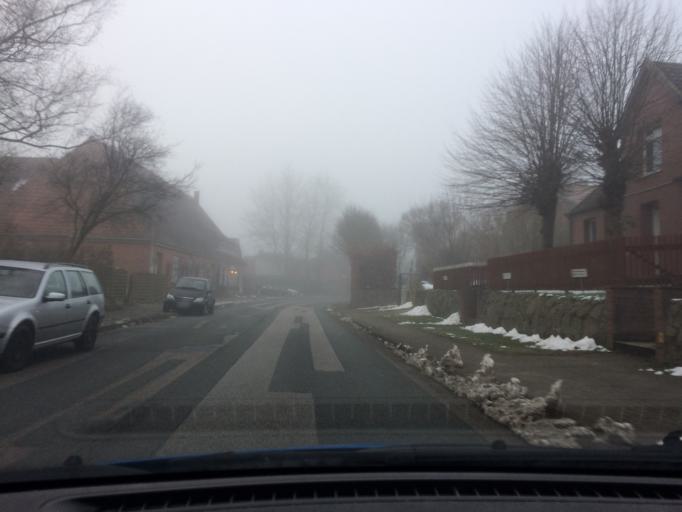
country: DE
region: Schleswig-Holstein
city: Kollow
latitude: 53.4597
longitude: 10.4608
